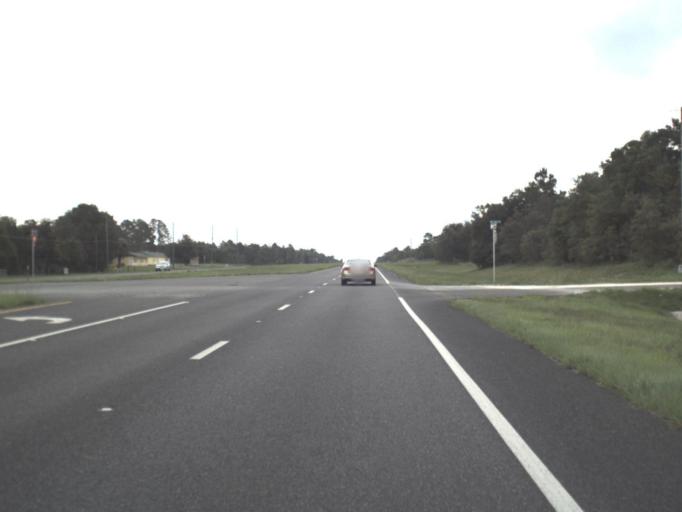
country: US
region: Florida
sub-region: Levy County
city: East Bronson
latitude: 29.4146
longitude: -82.5533
